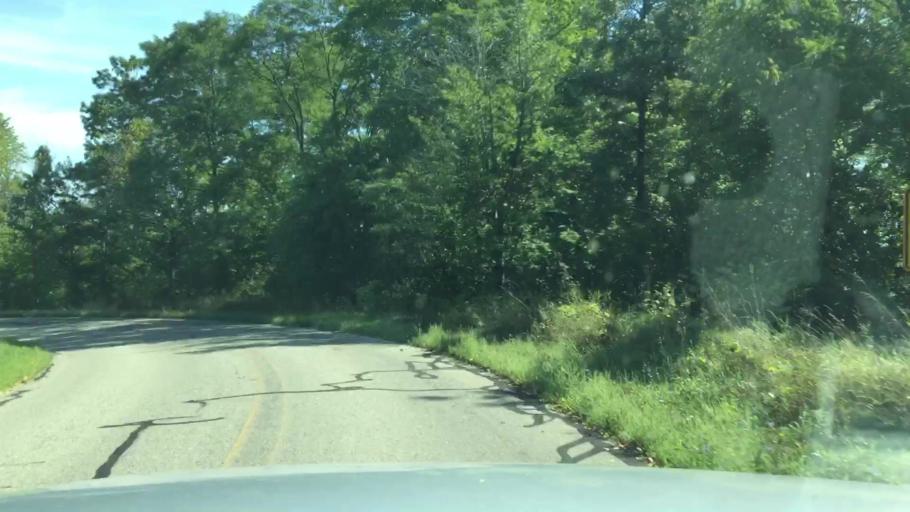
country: US
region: Michigan
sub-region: Lenawee County
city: Manitou Beach-Devils Lake
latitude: 42.0082
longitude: -84.3061
